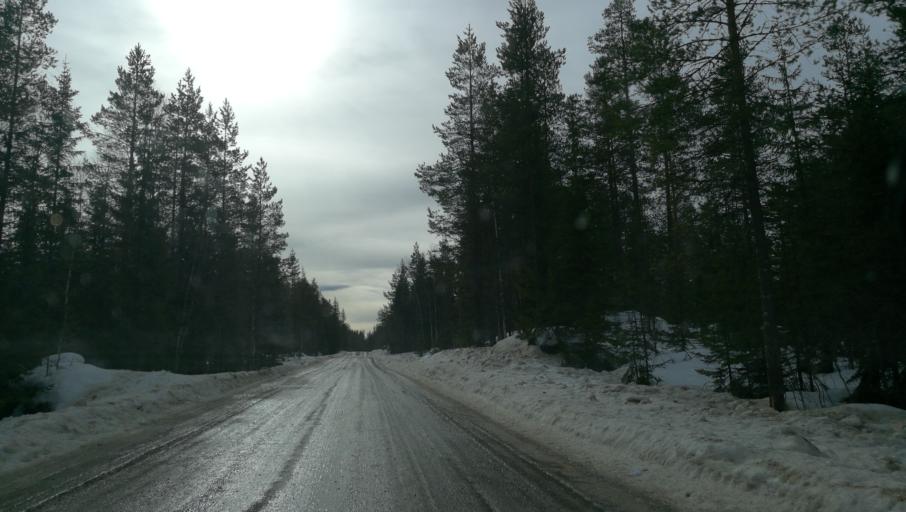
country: SE
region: Vaermland
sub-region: Torsby Kommun
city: Torsby
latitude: 60.6735
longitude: 12.8741
